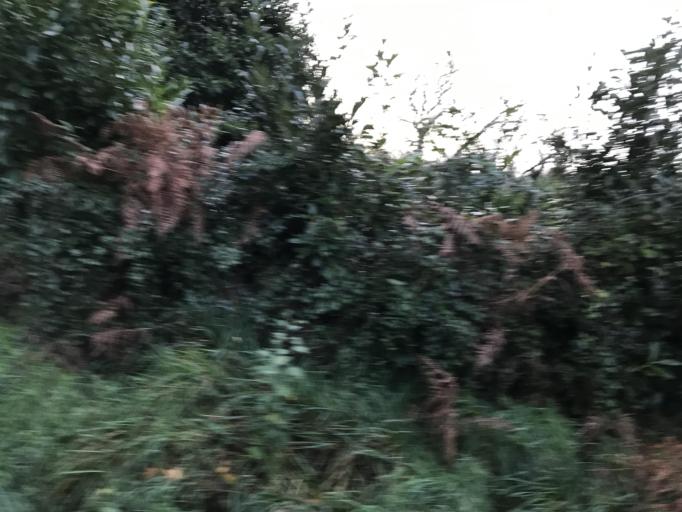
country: FR
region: Brittany
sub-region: Departement du Finistere
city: Logonna-Daoulas
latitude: 48.3173
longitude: -4.3119
